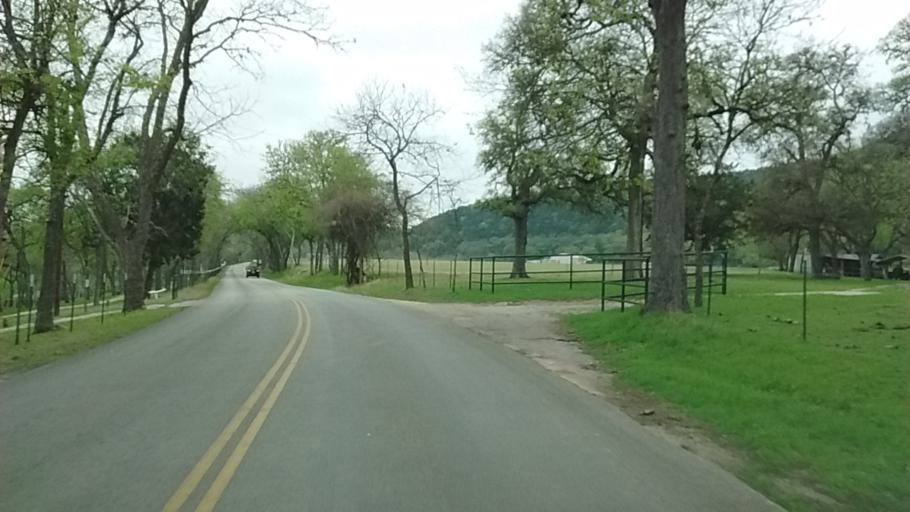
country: US
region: Texas
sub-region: Comal County
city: Canyon Lake
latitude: 29.8208
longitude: -98.1669
